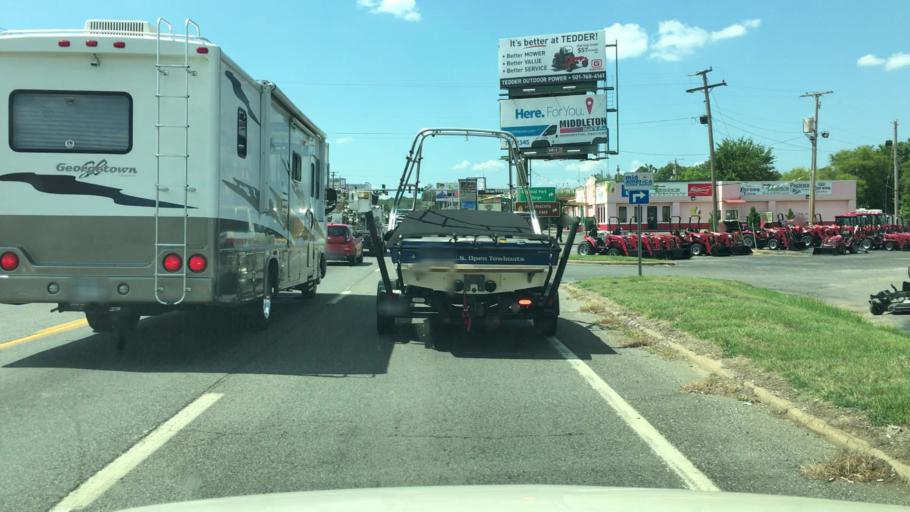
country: US
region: Arkansas
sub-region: Garland County
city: Piney
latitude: 34.5023
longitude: -93.1245
